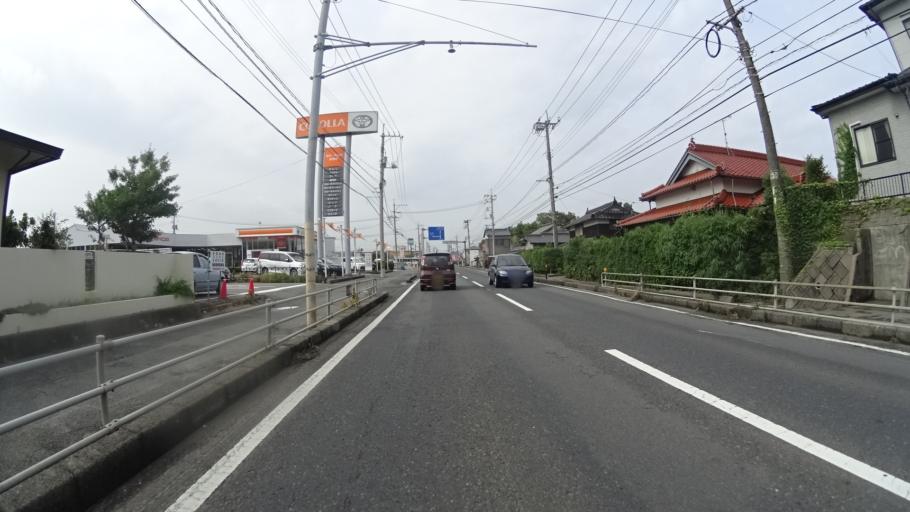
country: JP
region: Yamaguchi
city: Shimonoseki
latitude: 34.0333
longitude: 130.9129
